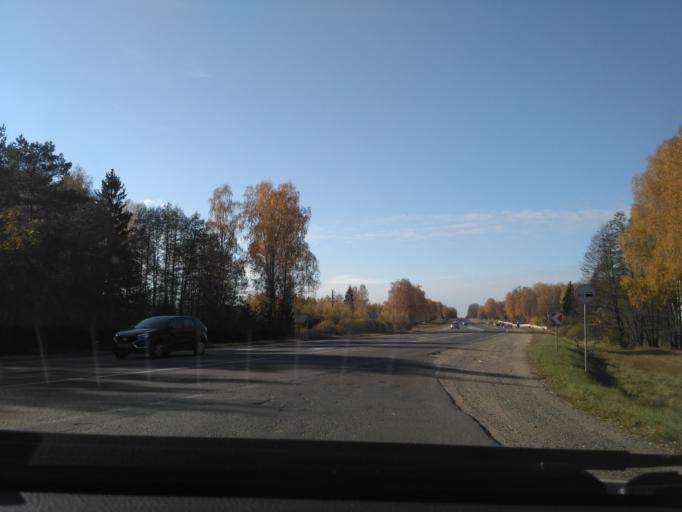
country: BY
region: Minsk
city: Horad Barysaw
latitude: 54.2556
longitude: 28.5724
